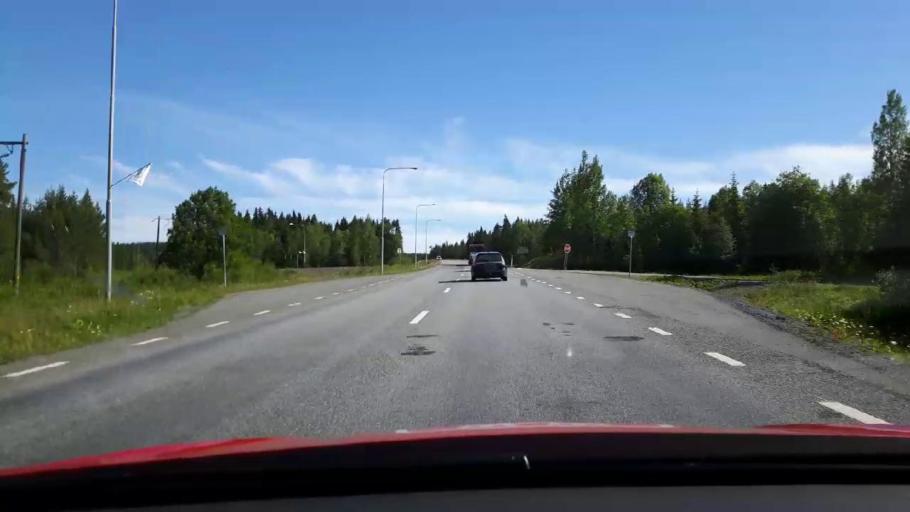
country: SE
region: Jaemtland
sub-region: OEstersunds Kommun
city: Lit
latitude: 63.3792
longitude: 14.8869
